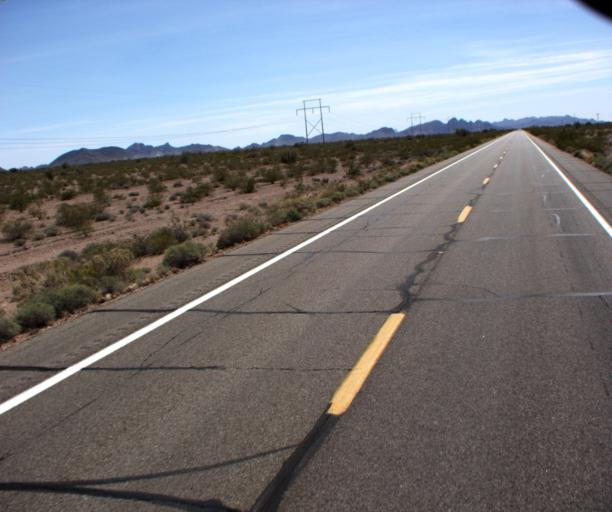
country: US
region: Arizona
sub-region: La Paz County
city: Quartzsite
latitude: 33.3965
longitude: -114.2172
